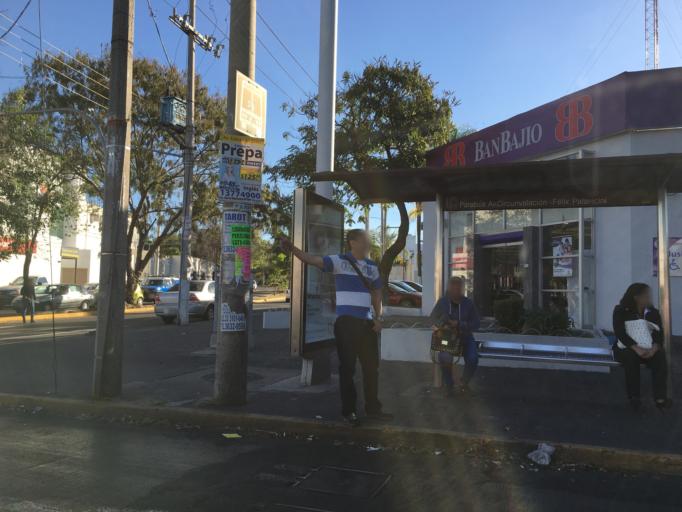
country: MX
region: Jalisco
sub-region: Zapopan
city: Zapopan
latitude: 20.7058
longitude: -103.3488
